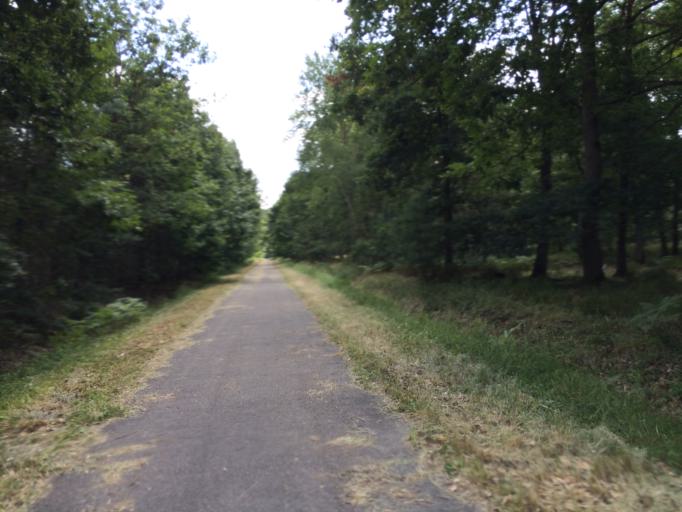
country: FR
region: Ile-de-France
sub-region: Departement de l'Essonne
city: Montgeron
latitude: 48.6854
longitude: 2.4581
